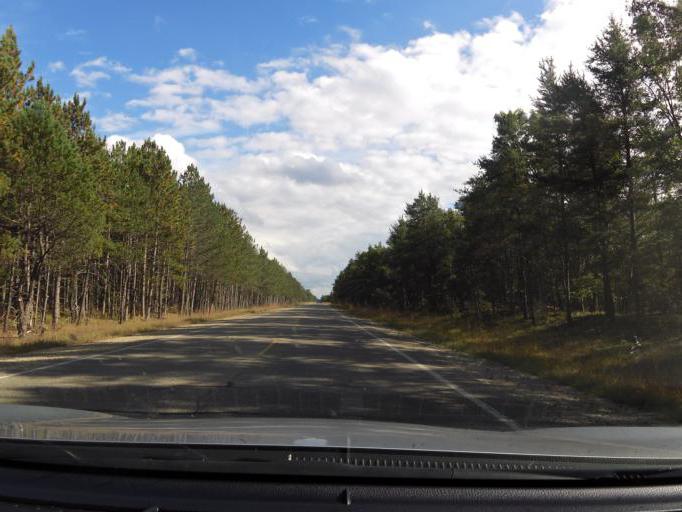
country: US
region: Michigan
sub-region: Roscommon County
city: Roscommon
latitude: 44.4806
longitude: -84.5622
